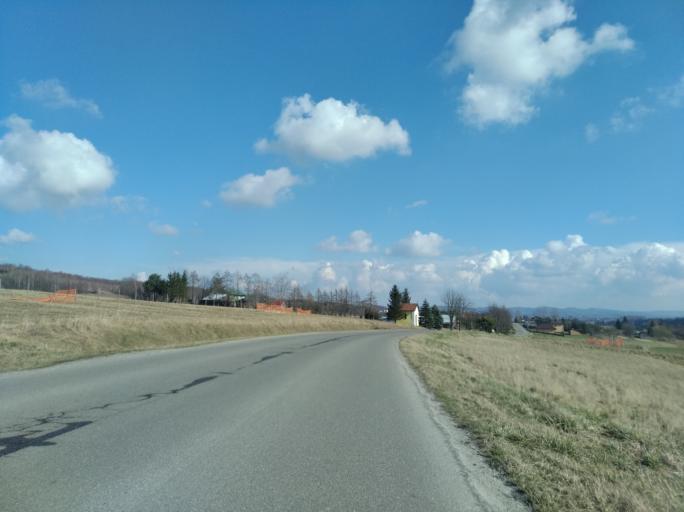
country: PL
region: Subcarpathian Voivodeship
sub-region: Powiat strzyzowski
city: Frysztak
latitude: 49.8500
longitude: 21.5300
